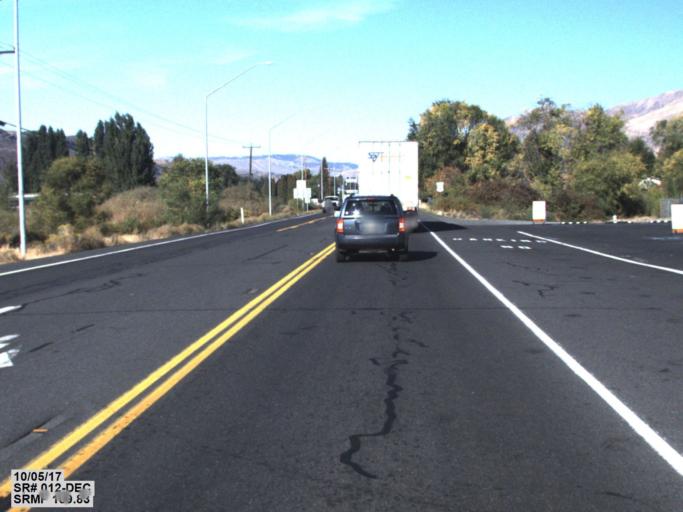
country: US
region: Washington
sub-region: Yakima County
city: Tieton
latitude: 46.7284
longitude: -120.7010
